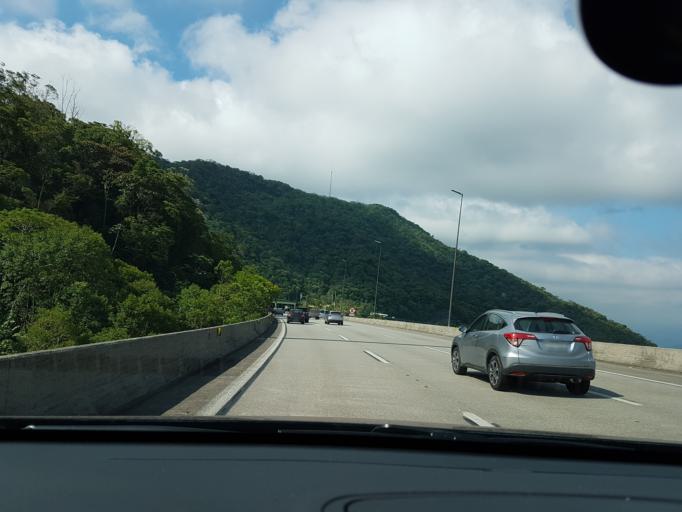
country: BR
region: Sao Paulo
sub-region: Cubatao
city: Cubatao
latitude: -23.9224
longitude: -46.5321
